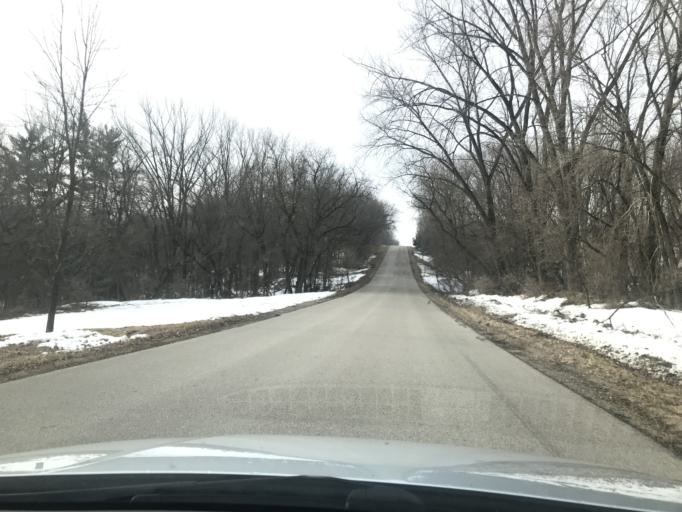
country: US
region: Wisconsin
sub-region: Oconto County
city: Oconto Falls
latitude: 44.8655
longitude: -88.1466
